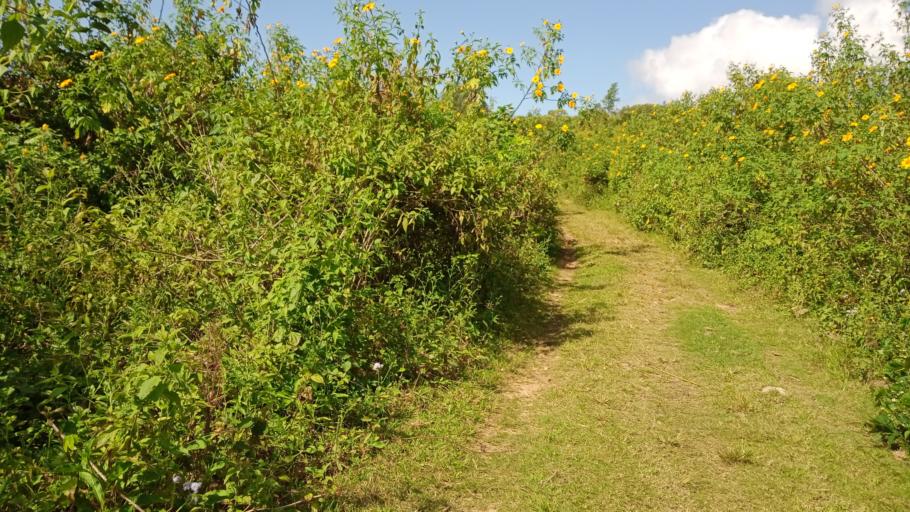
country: LA
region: Xiangkhoang
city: Phonsavan
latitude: 19.1168
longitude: 102.9225
